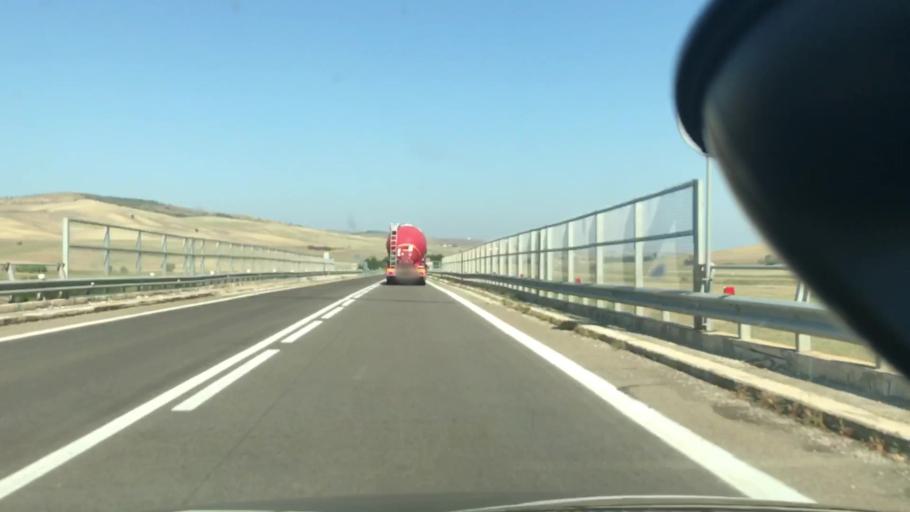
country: IT
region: Basilicate
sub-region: Provincia di Matera
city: Irsina
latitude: 40.7894
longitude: 16.2863
